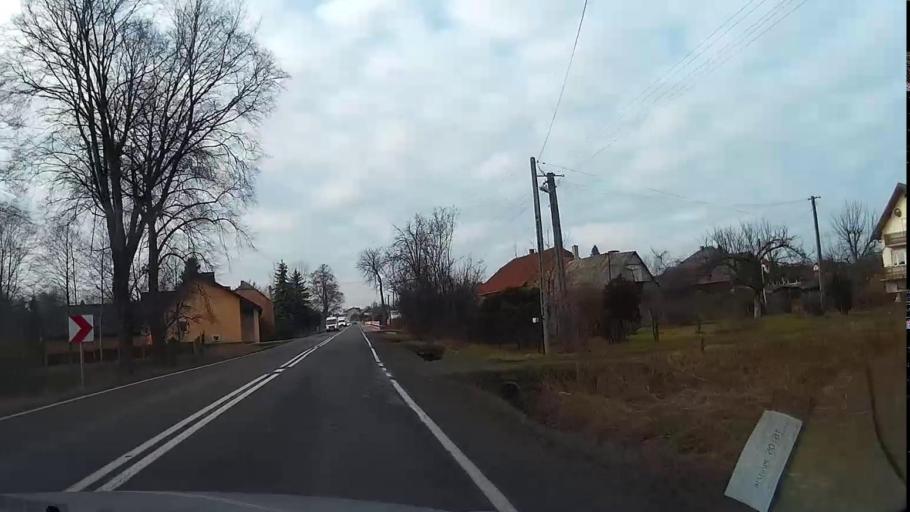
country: PL
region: Lesser Poland Voivodeship
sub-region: Powiat chrzanowski
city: Brodla
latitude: 50.0409
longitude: 19.5953
